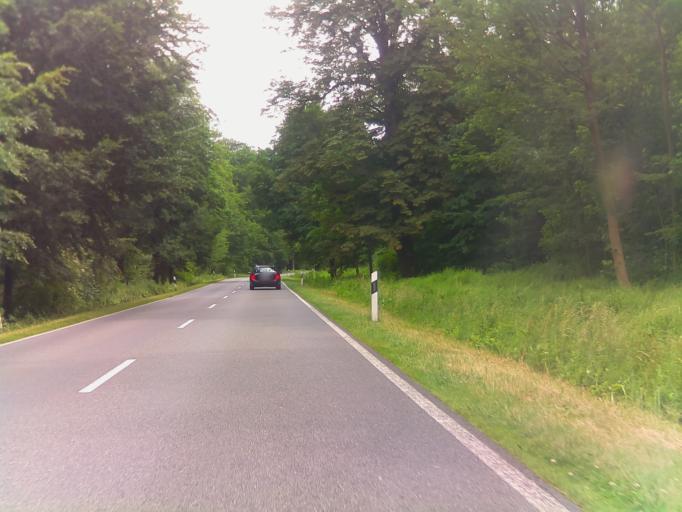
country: DE
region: Lower Saxony
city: Springe
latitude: 52.1863
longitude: 9.5850
